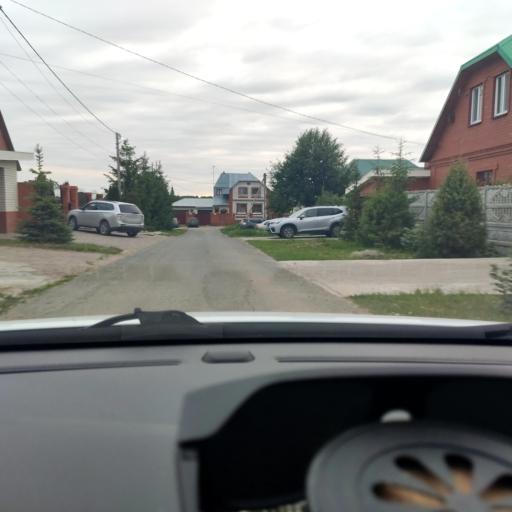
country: RU
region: Tatarstan
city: Vysokaya Gora
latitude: 55.9143
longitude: 49.3340
